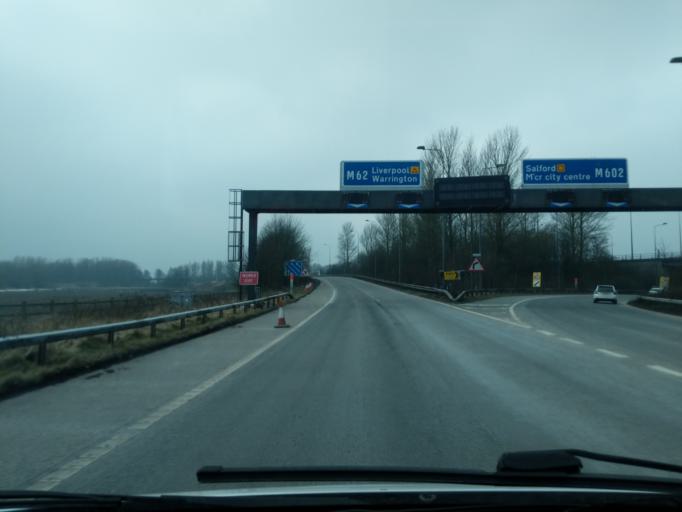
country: GB
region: England
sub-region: Manchester
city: Swinton
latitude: 53.4855
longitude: -2.3787
